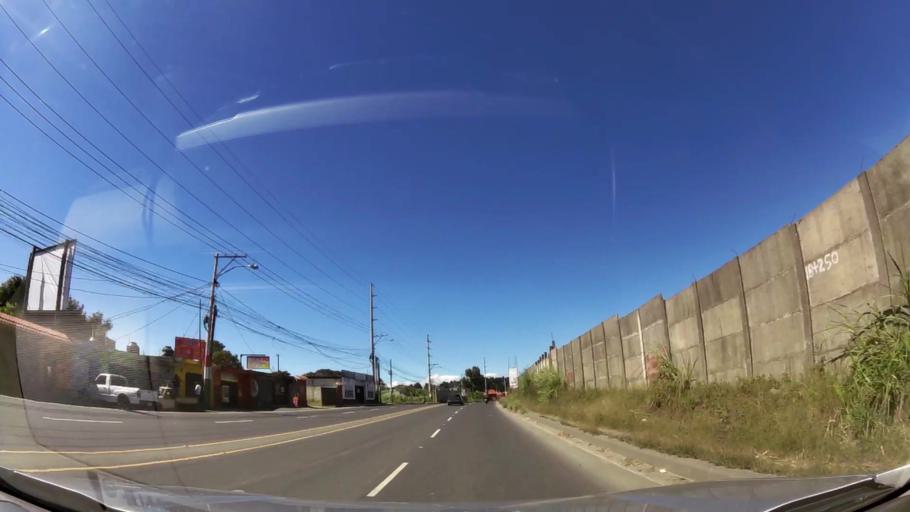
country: GT
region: Guatemala
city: San Jose Pinula
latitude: 14.5432
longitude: -90.4388
